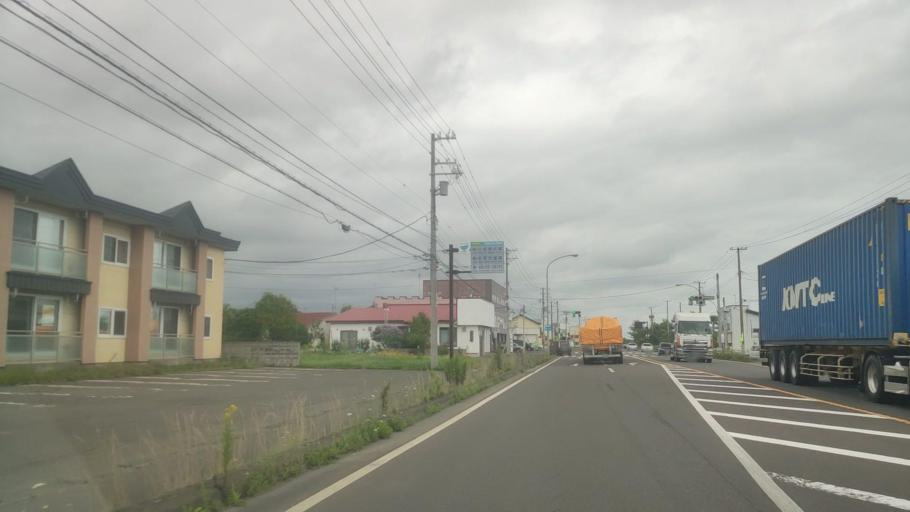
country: JP
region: Hokkaido
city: Shiraoi
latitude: 42.5181
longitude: 141.3034
